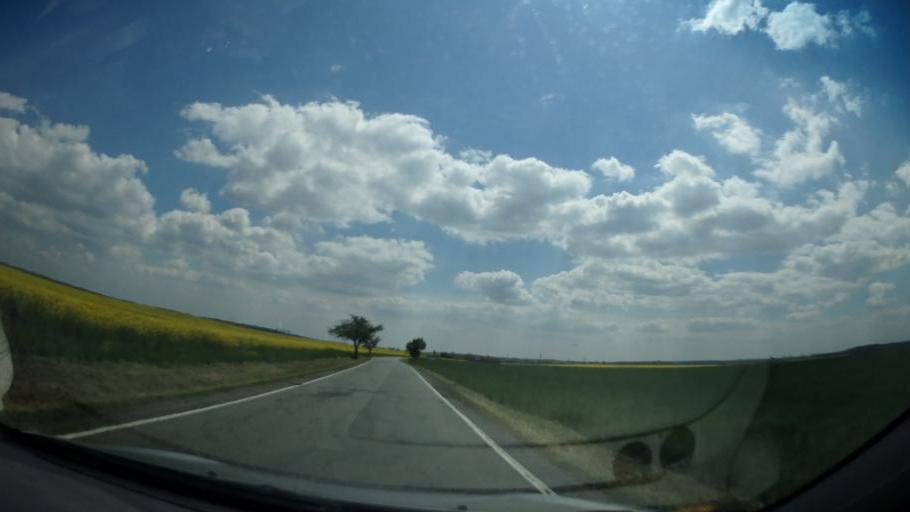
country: CZ
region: Vysocina
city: Hrotovice
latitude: 49.1424
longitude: 16.0774
